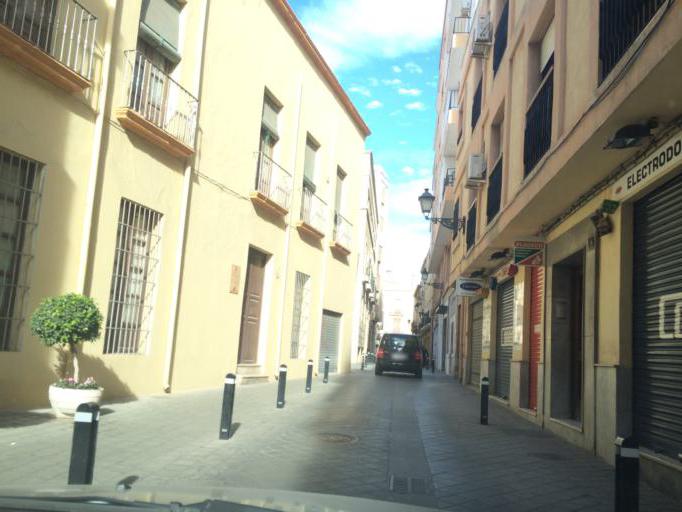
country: ES
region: Andalusia
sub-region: Provincia de Almeria
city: Almeria
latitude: 36.8397
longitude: -2.4668
